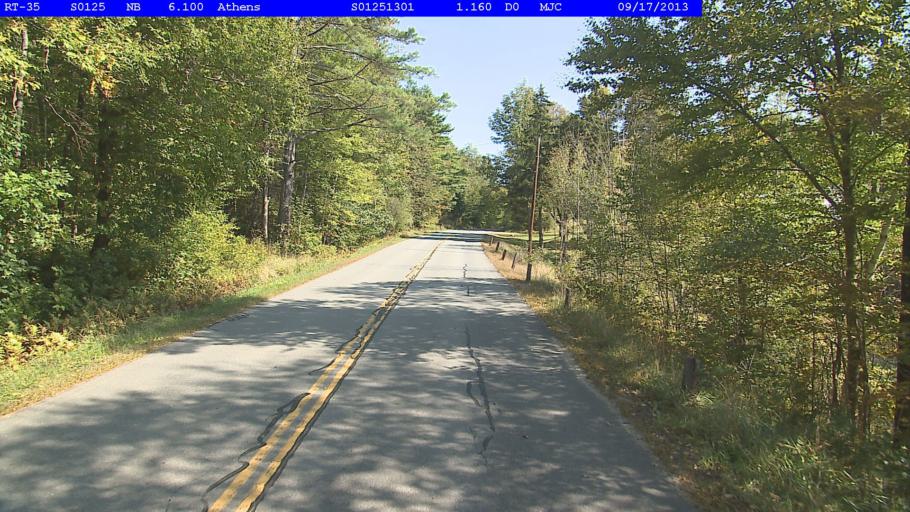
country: US
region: Vermont
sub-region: Windham County
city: Rockingham
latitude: 43.1169
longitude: -72.6079
